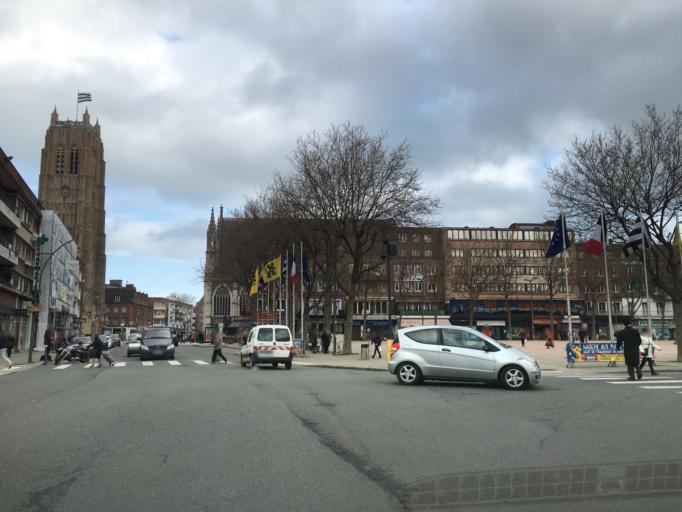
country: FR
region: Nord-Pas-de-Calais
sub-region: Departement du Nord
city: Dunkerque
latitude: 51.0343
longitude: 2.3768
